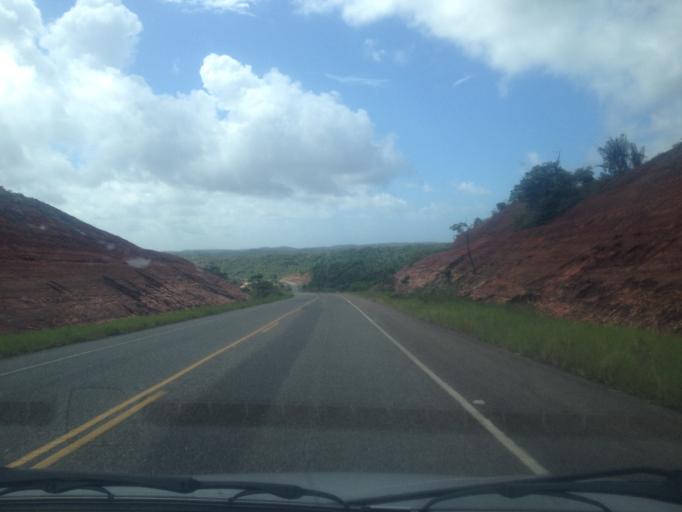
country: BR
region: Bahia
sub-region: Conde
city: Conde
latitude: -12.0792
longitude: -37.7596
